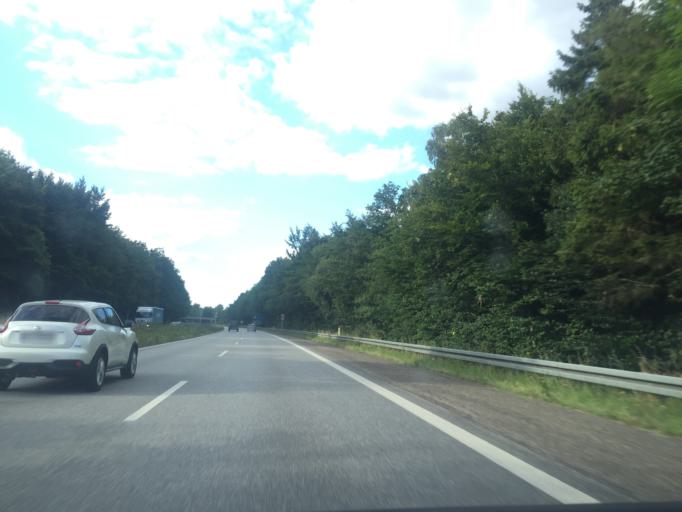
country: DK
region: Zealand
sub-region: Koge Kommune
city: Ejby
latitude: 55.4482
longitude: 12.1225
